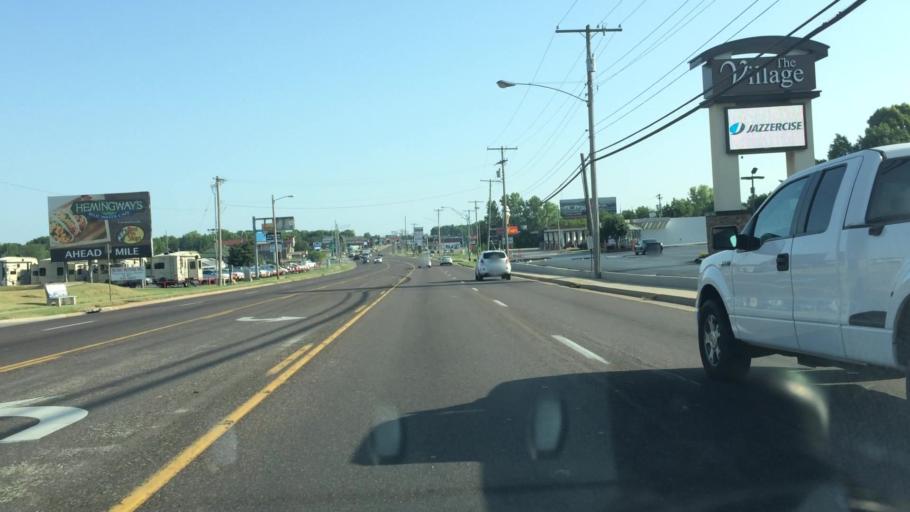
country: US
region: Missouri
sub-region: Greene County
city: Springfield
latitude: 37.1637
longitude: -93.2953
